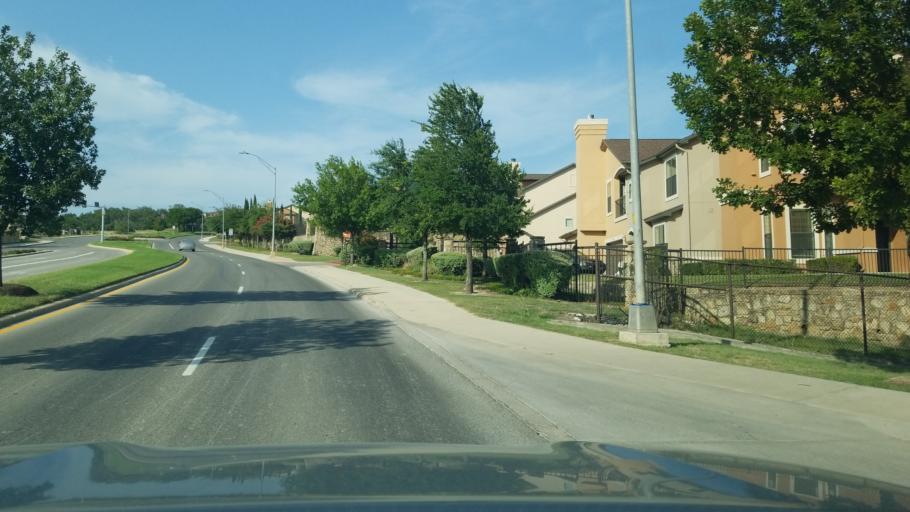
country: US
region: Texas
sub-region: Bexar County
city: Hollywood Park
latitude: 29.6466
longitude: -98.4663
